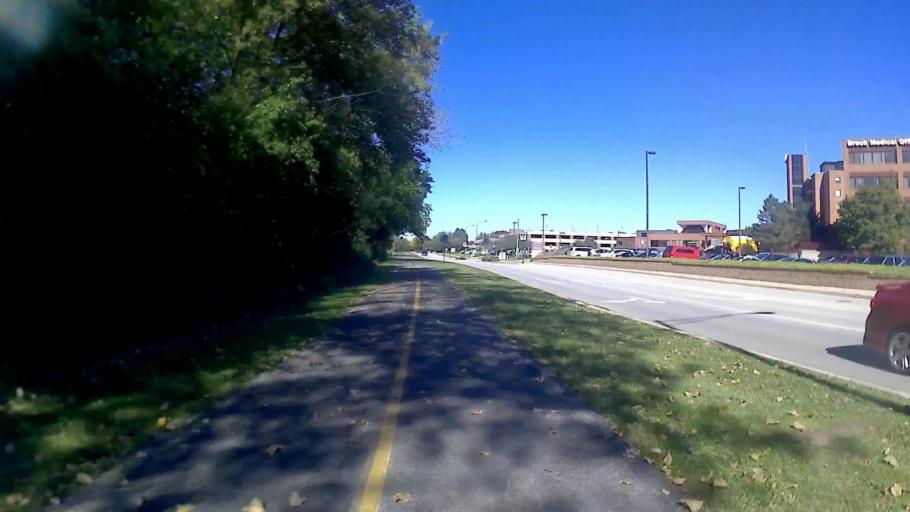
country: US
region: Illinois
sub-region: DuPage County
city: Itasca
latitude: 42.0037
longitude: -88.0185
